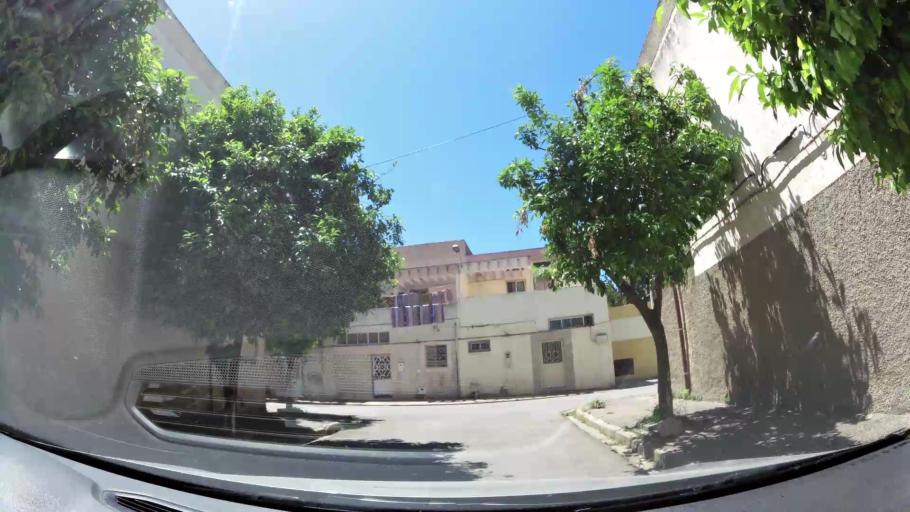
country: MA
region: Fes-Boulemane
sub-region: Fes
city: Fes
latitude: 34.0221
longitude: -5.0041
